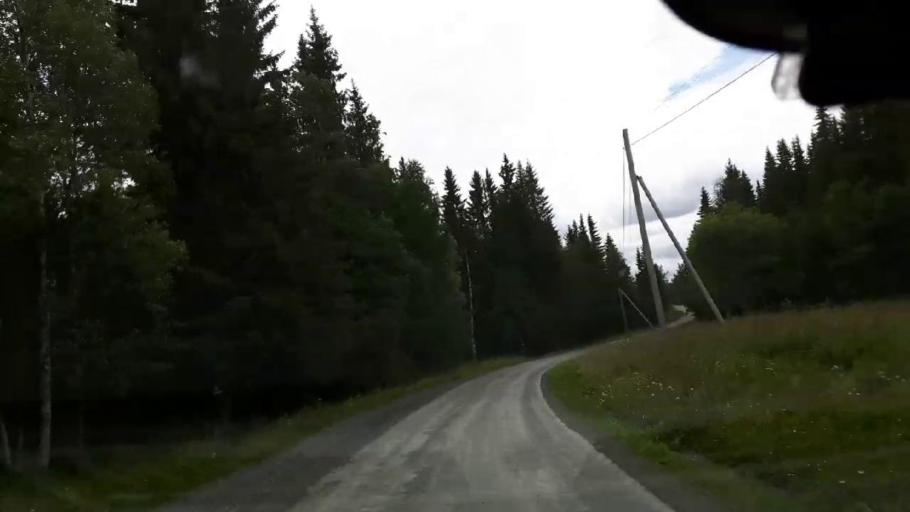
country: SE
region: Jaemtland
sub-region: Krokoms Kommun
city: Valla
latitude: 63.6969
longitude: 13.8724
